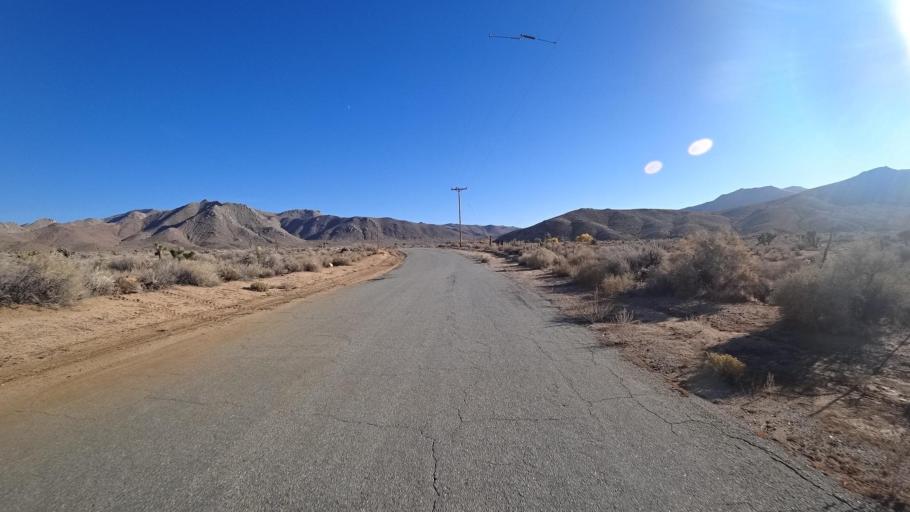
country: US
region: California
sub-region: Kern County
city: Weldon
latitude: 35.5525
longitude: -118.2136
